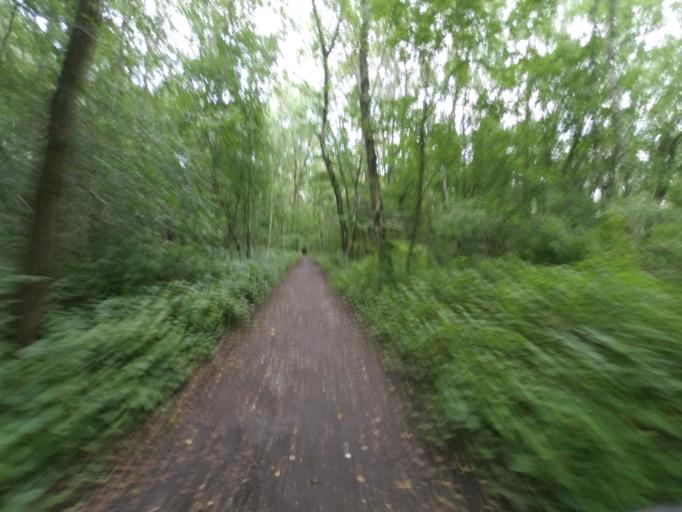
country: DE
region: Schleswig-Holstein
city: Oststeinbek
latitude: 53.5069
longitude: 10.1703
